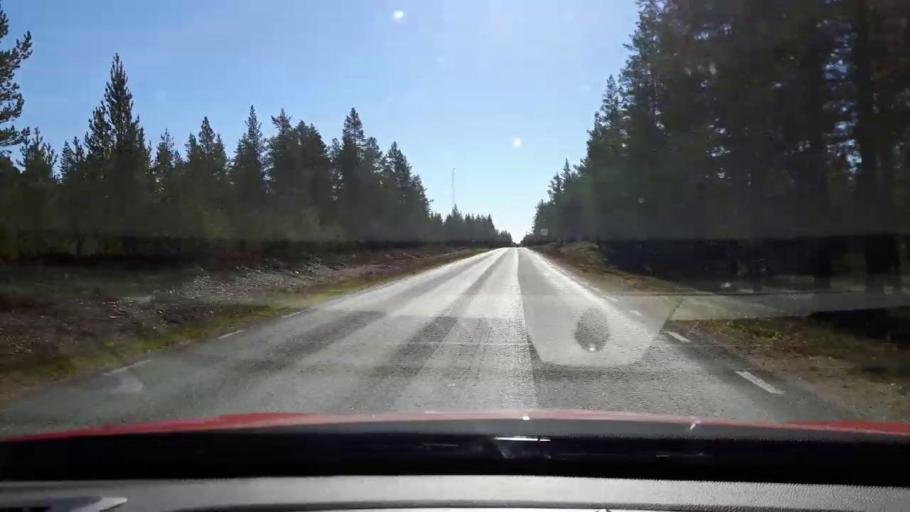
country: SE
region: Jaemtland
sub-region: Harjedalens Kommun
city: Sveg
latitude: 62.4131
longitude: 13.9175
